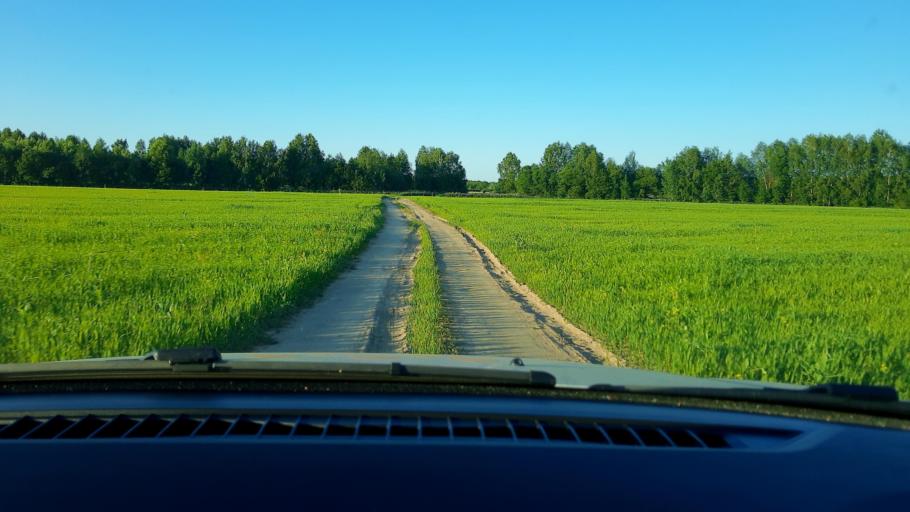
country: RU
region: Nizjnij Novgorod
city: Kstovo
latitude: 56.3052
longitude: 44.2623
